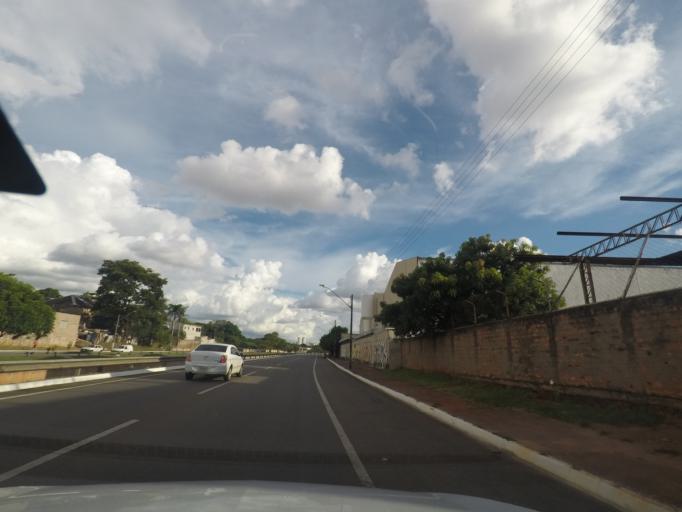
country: BR
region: Goias
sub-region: Goiania
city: Goiania
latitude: -16.6790
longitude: -49.2938
